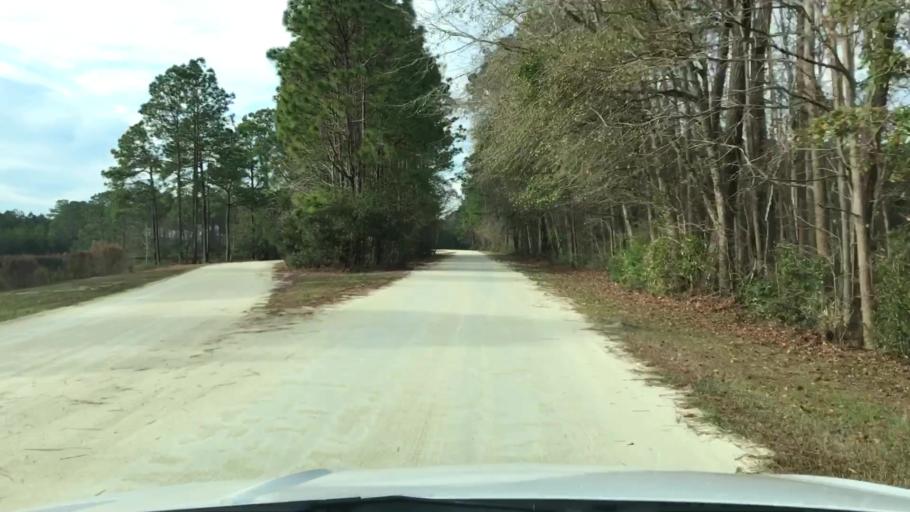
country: US
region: South Carolina
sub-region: Charleston County
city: Isle of Palms
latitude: 32.9051
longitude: -79.7219
